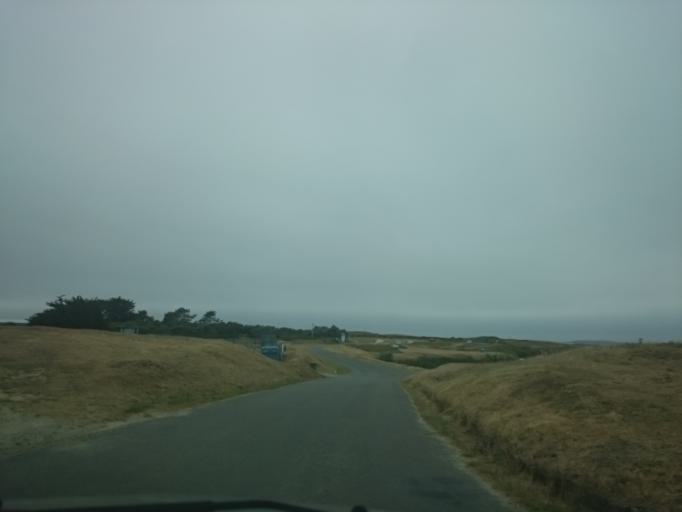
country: FR
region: Brittany
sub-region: Departement du Finistere
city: Saint-Pabu
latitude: 48.5748
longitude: -4.6259
